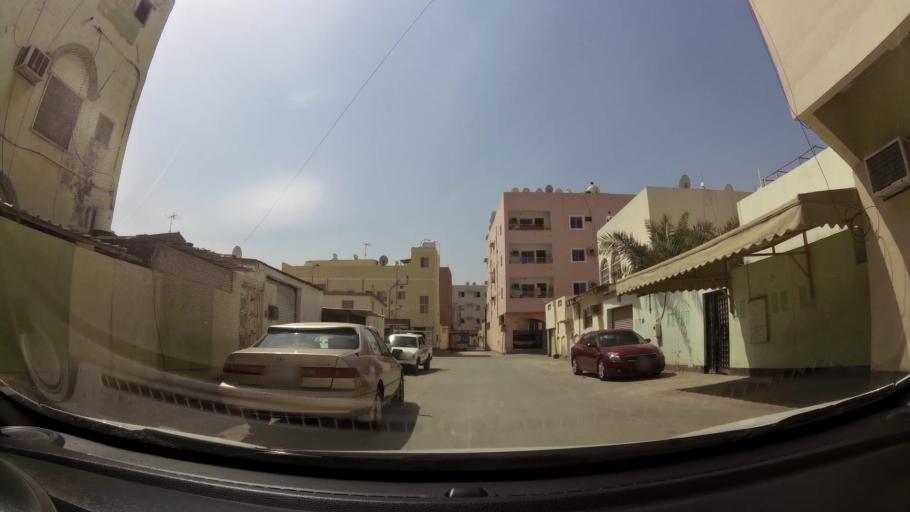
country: BH
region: Manama
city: Jidd Hafs
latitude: 26.2171
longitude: 50.4515
